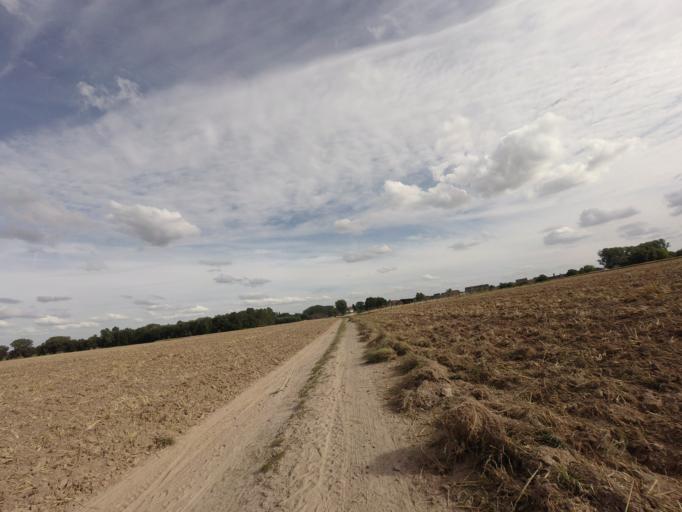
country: BE
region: Flanders
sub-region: Provincie Vlaams-Brabant
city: Grimbergen
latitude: 50.9583
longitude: 4.3804
